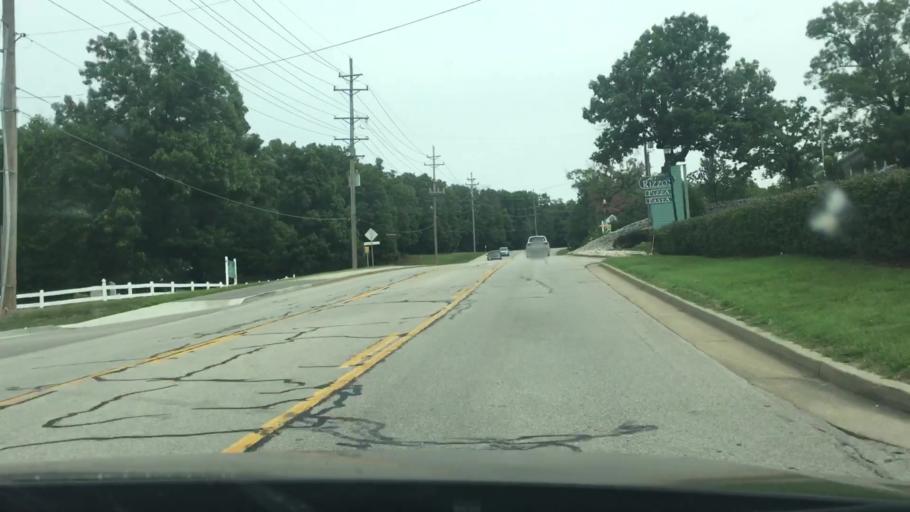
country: US
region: Missouri
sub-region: Camden County
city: Four Seasons
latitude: 38.1925
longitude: -92.6790
